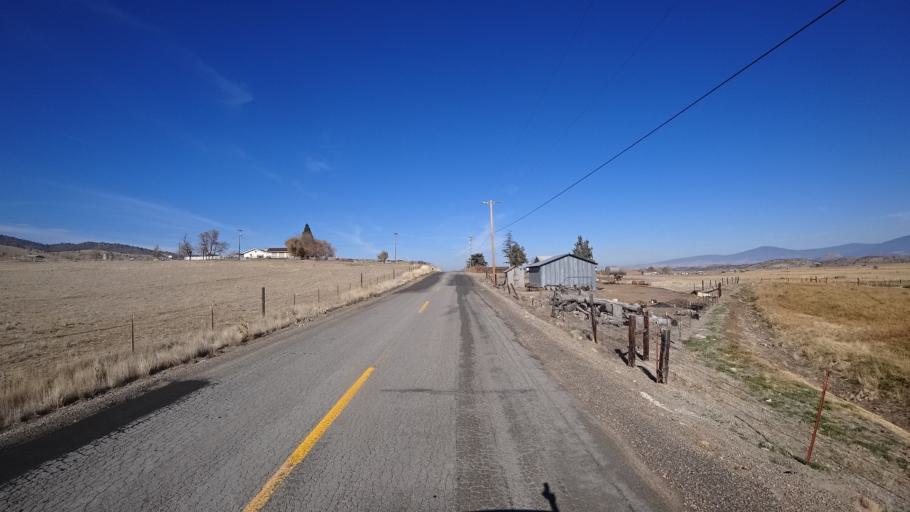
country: US
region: California
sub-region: Siskiyou County
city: Montague
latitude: 41.6067
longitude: -122.5301
